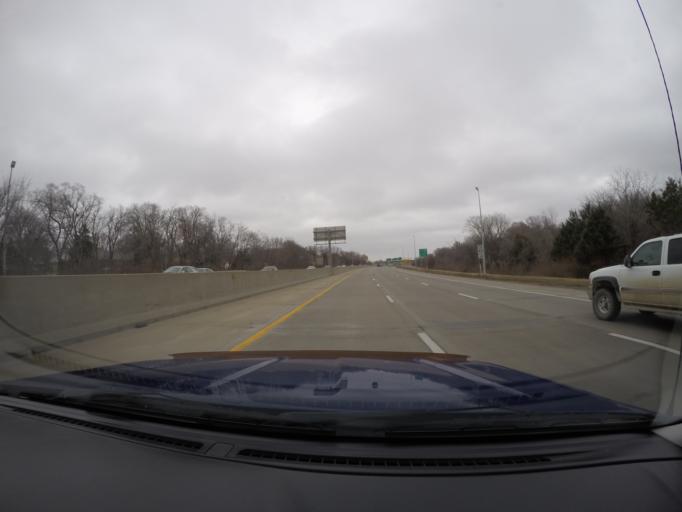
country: US
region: Kansas
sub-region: Shawnee County
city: Topeka
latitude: 39.0634
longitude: -95.7386
